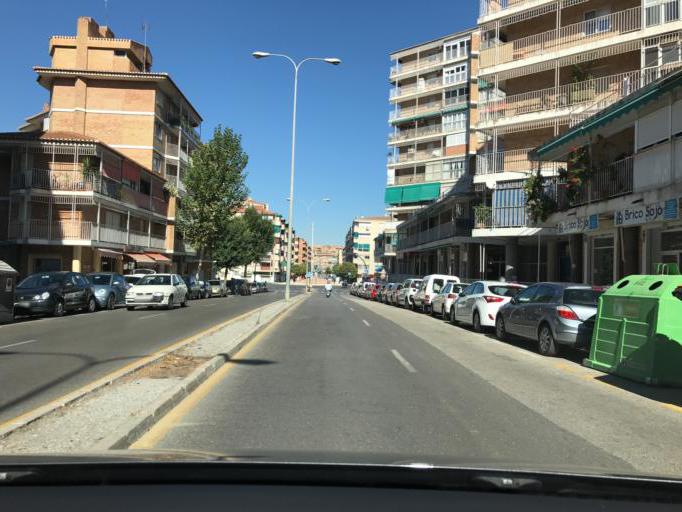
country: ES
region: Andalusia
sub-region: Provincia de Granada
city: Armilla
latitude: 37.1614
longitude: -3.6016
